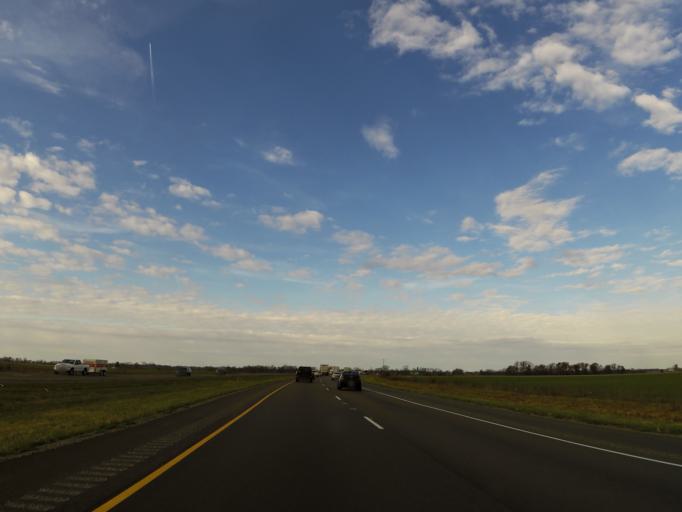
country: US
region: Illinois
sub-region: Washington County
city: Okawville
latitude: 38.4317
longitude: -89.5096
